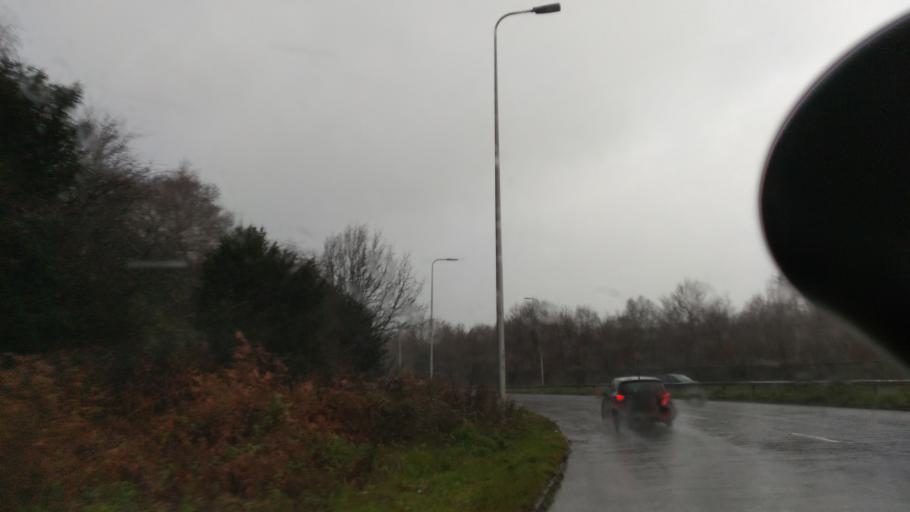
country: GB
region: England
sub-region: West Sussex
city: Fontwell
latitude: 50.8567
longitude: -0.6421
